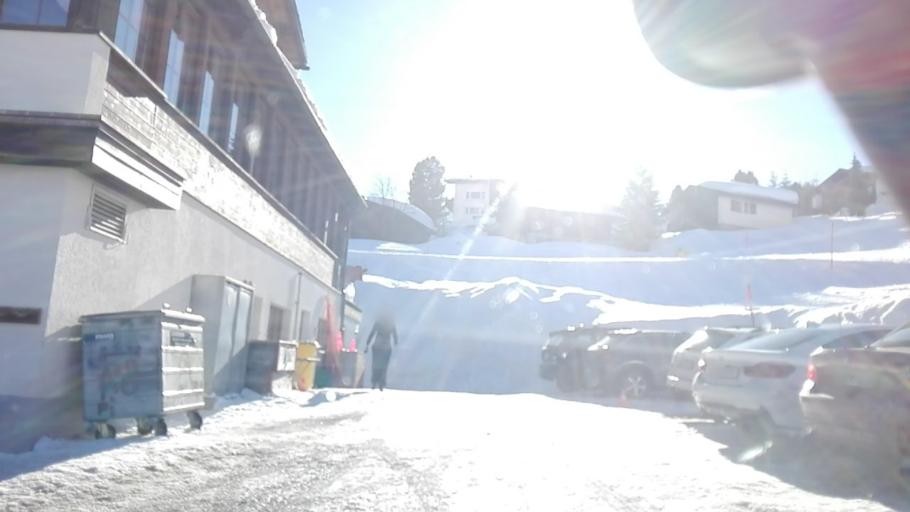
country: CH
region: Grisons
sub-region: Plessur District
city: Arosa
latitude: 46.7757
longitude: 9.6597
